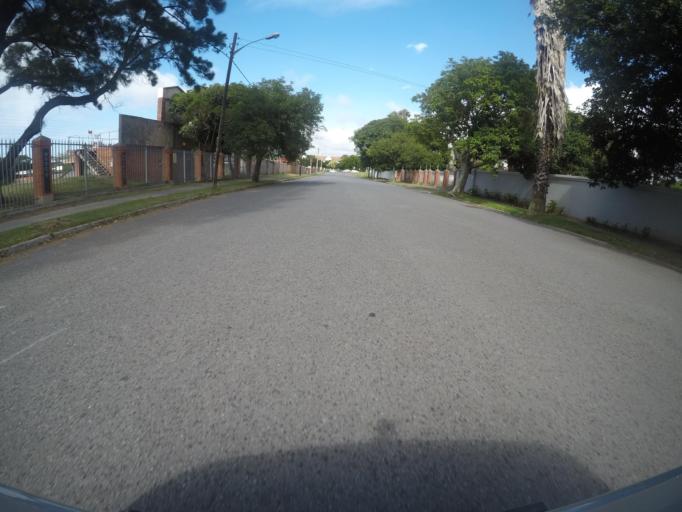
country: ZA
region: Eastern Cape
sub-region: Buffalo City Metropolitan Municipality
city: East London
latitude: -32.9938
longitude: 27.8982
